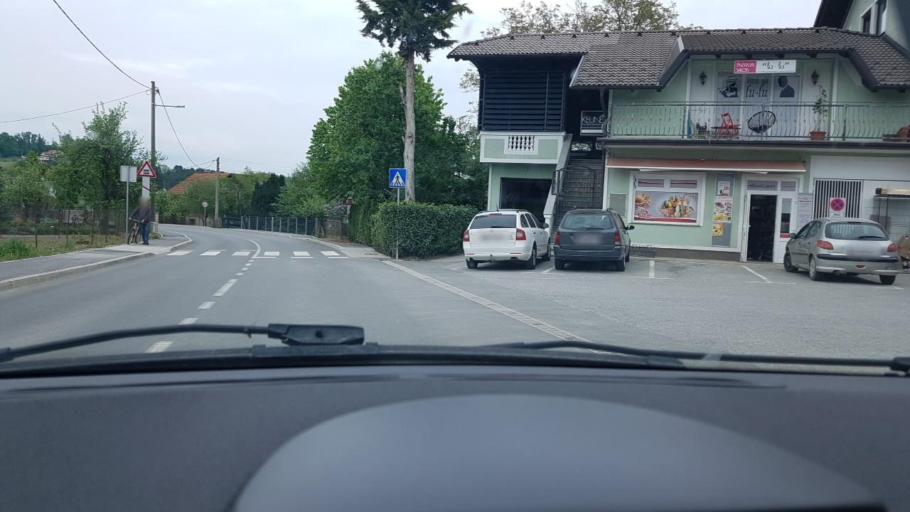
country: HR
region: Krapinsko-Zagorska
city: Selnica
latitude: 45.9833
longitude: 16.0003
